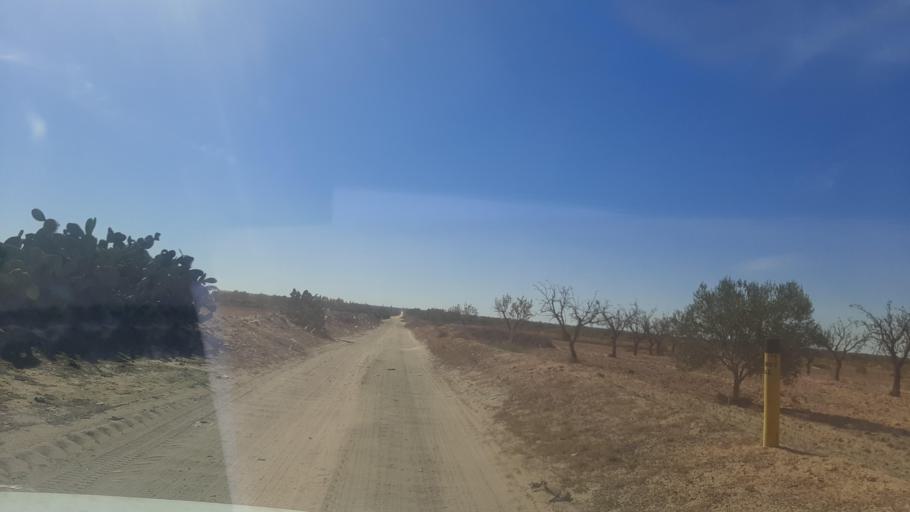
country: TN
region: Safaqis
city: Sfax
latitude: 34.8471
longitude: 10.5614
